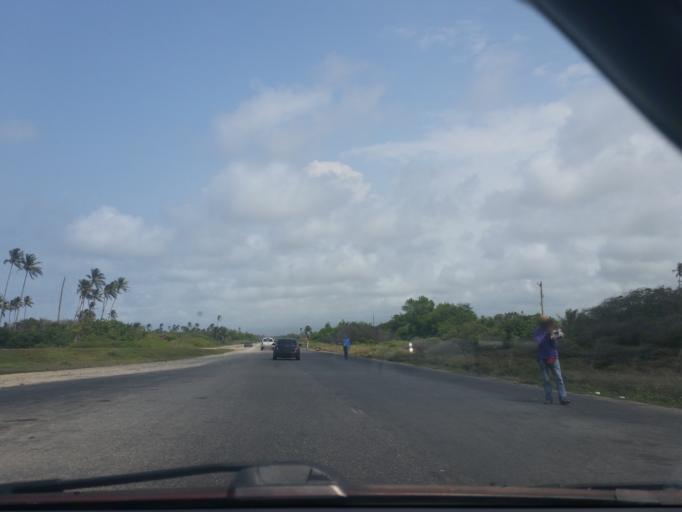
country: VE
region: Carabobo
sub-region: Municipio Juan Jose Mora
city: Moron
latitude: 10.6013
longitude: -68.2548
